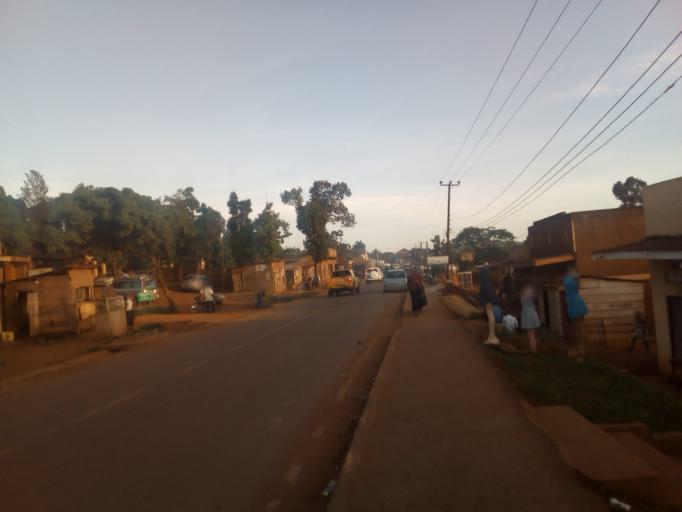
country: UG
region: Central Region
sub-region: Wakiso District
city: Kajansi
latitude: 0.2451
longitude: 32.5718
